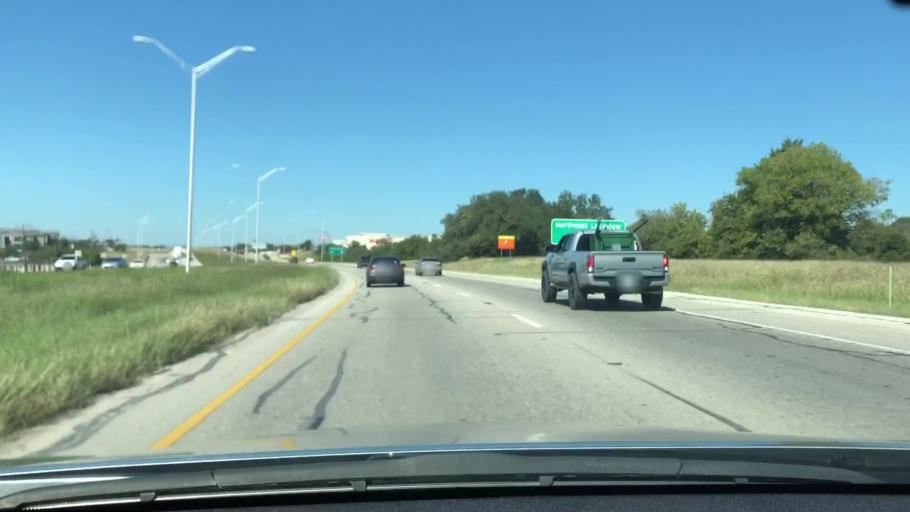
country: US
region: Texas
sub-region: Bexar County
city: Universal City
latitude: 29.5421
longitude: -98.3080
